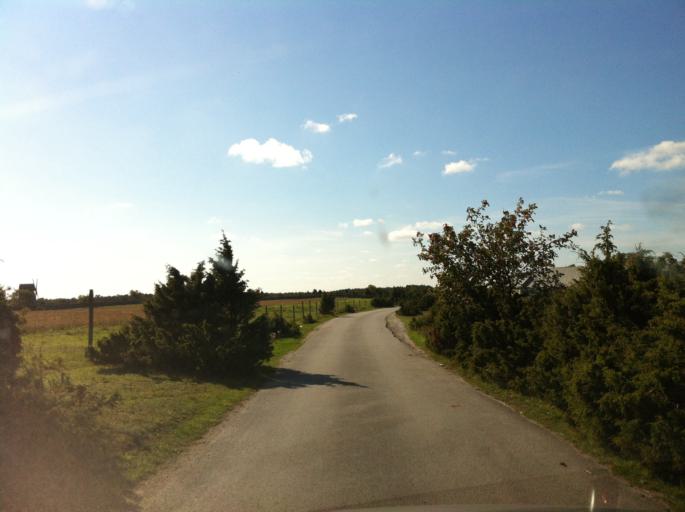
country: SE
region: Gotland
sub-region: Gotland
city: Slite
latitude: 57.9855
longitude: 19.1663
